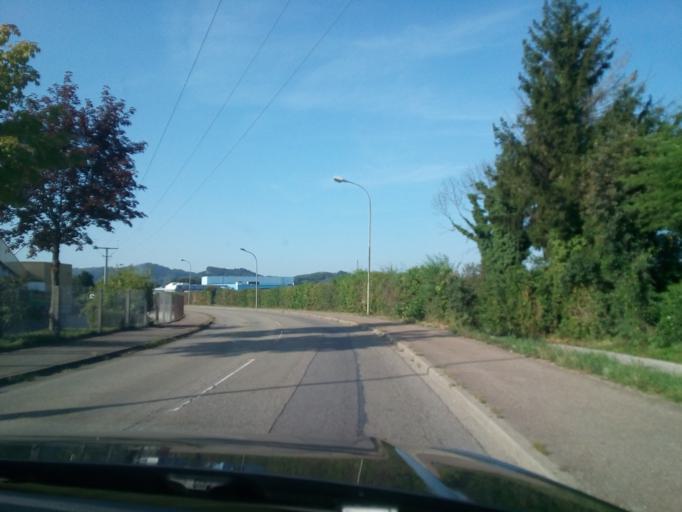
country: DE
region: Baden-Wuerttemberg
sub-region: Freiburg Region
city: Oberkirch
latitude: 48.5408
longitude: 8.0641
